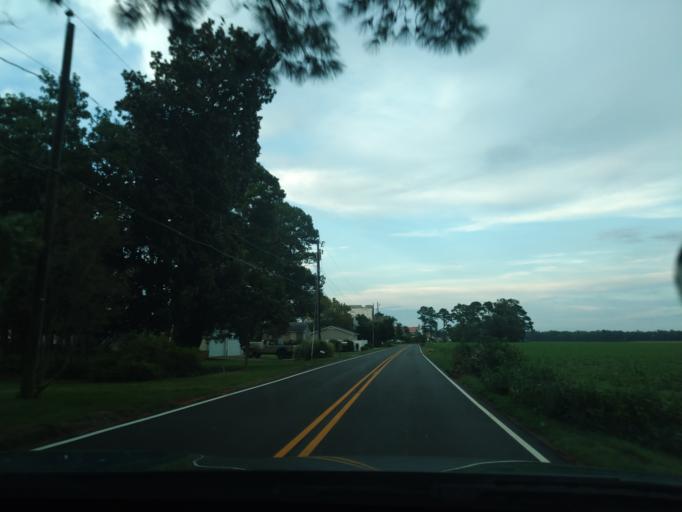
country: US
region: North Carolina
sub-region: Chowan County
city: Edenton
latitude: 35.9356
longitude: -76.6387
